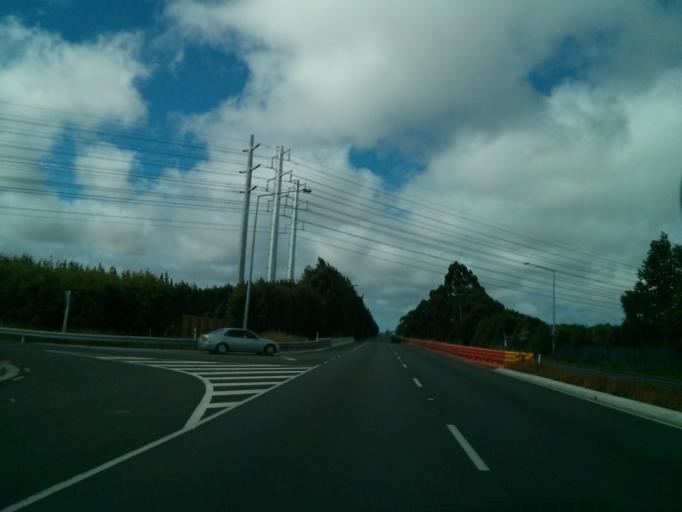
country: NZ
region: Canterbury
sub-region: Selwyn District
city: Prebbleton
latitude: -43.5126
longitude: 172.5385
